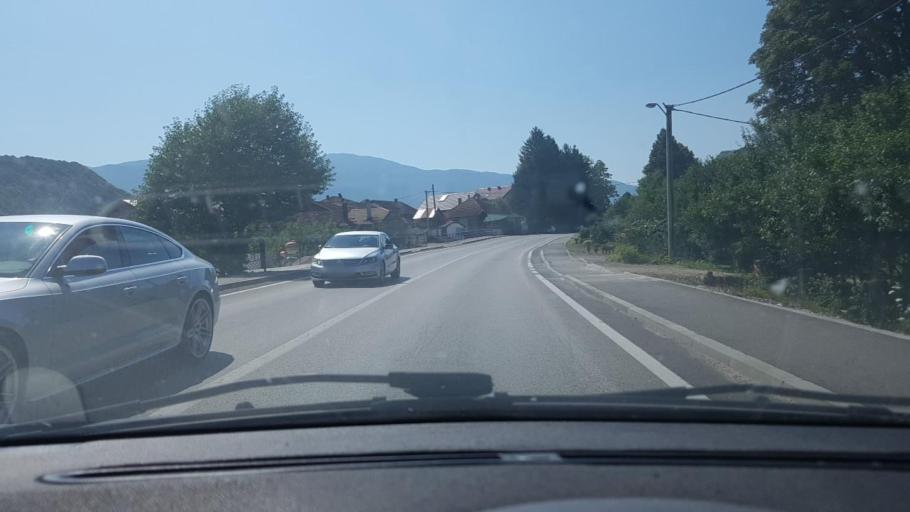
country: BA
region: Federation of Bosnia and Herzegovina
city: Bihac
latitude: 44.8072
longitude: 15.8884
